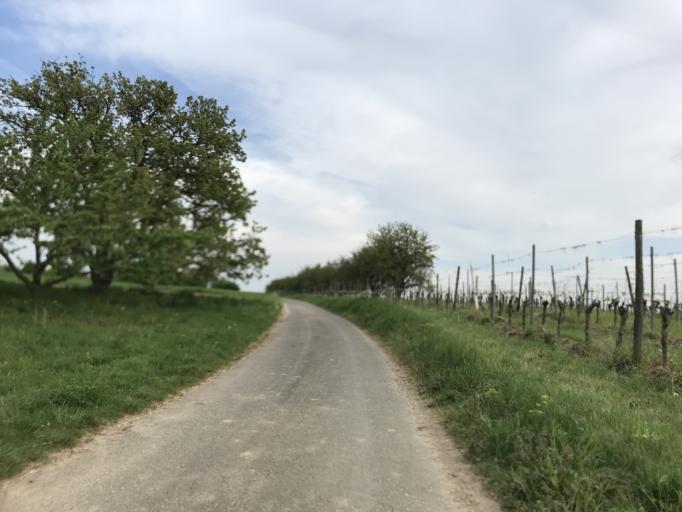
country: DE
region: Rheinland-Pfalz
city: Schwabenheim
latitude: 49.9468
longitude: 8.0940
